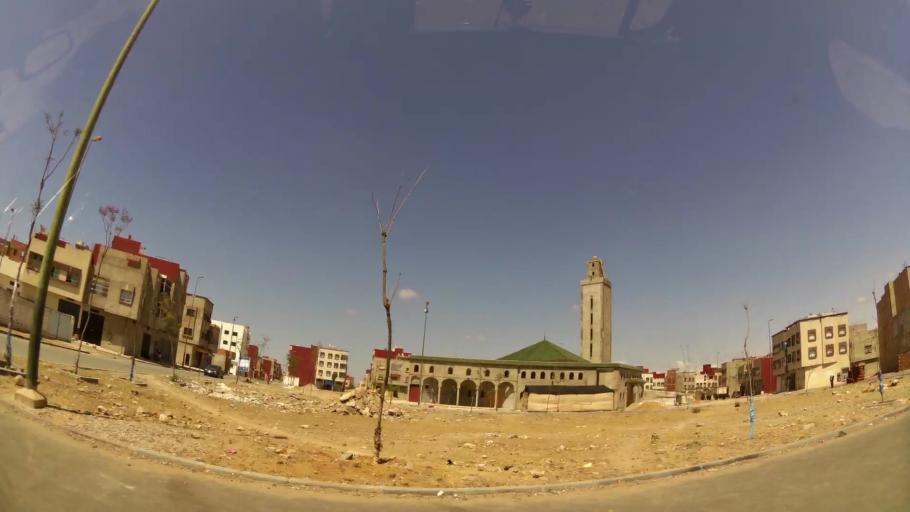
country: MA
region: Gharb-Chrarda-Beni Hssen
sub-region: Kenitra Province
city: Kenitra
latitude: 34.2419
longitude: -6.5398
